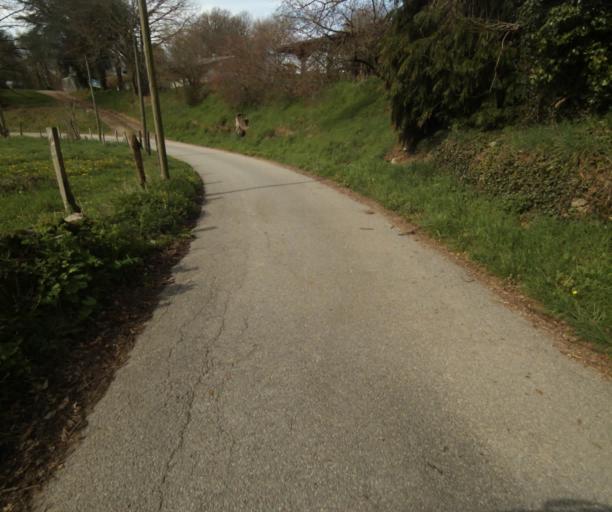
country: FR
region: Limousin
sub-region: Departement de la Correze
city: Correze
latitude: 45.3550
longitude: 1.8612
